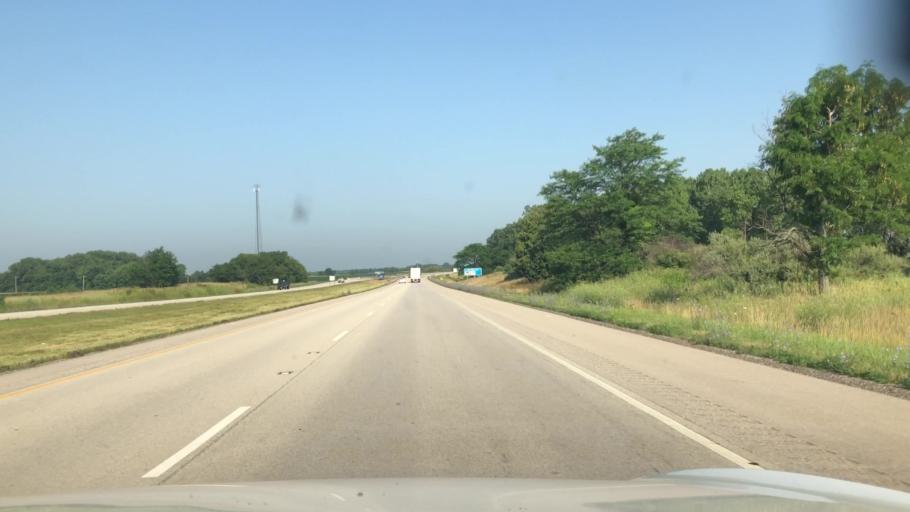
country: US
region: Illinois
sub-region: De Witt County
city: Farmer City
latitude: 40.2372
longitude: -88.5998
